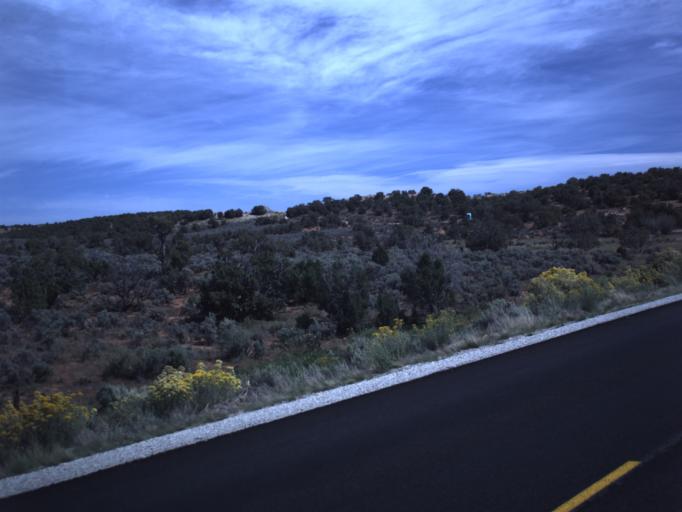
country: US
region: Utah
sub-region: San Juan County
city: Blanding
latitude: 37.5759
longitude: -109.5330
